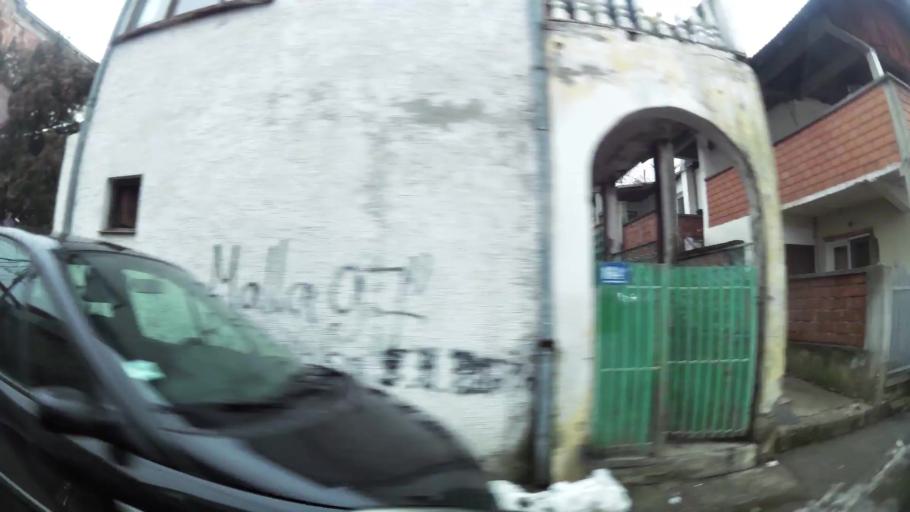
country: RS
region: Central Serbia
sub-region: Belgrade
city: Zvezdara
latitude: 44.7758
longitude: 20.5077
